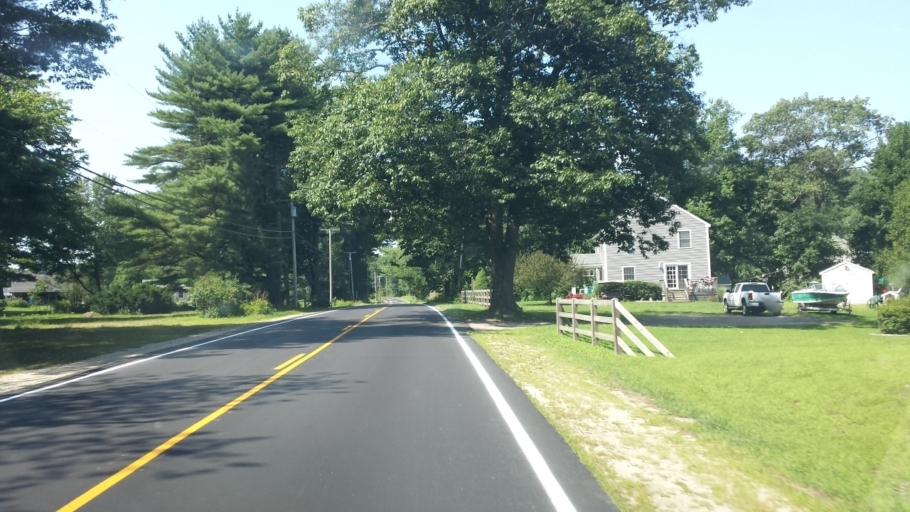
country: US
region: Maine
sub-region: York County
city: Arundel
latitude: 43.4169
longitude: -70.5017
